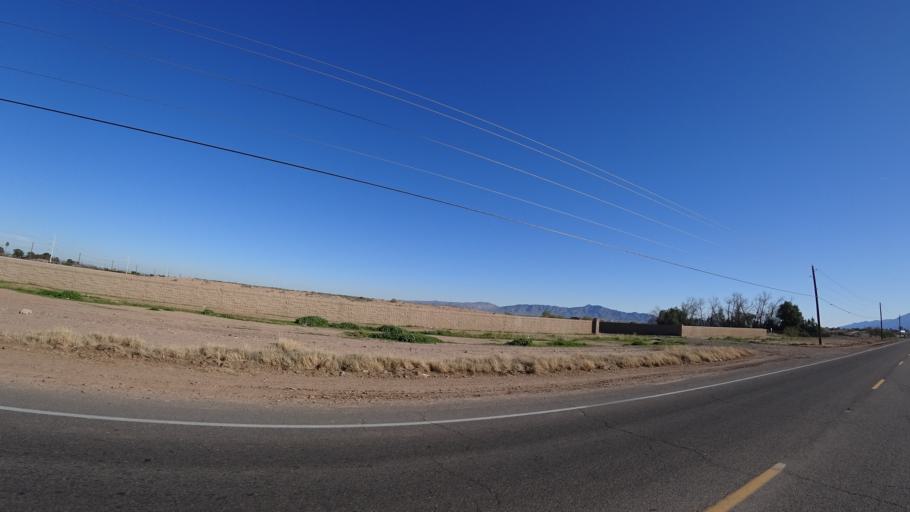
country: US
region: Arizona
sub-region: Maricopa County
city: Laveen
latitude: 33.4065
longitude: -112.2042
